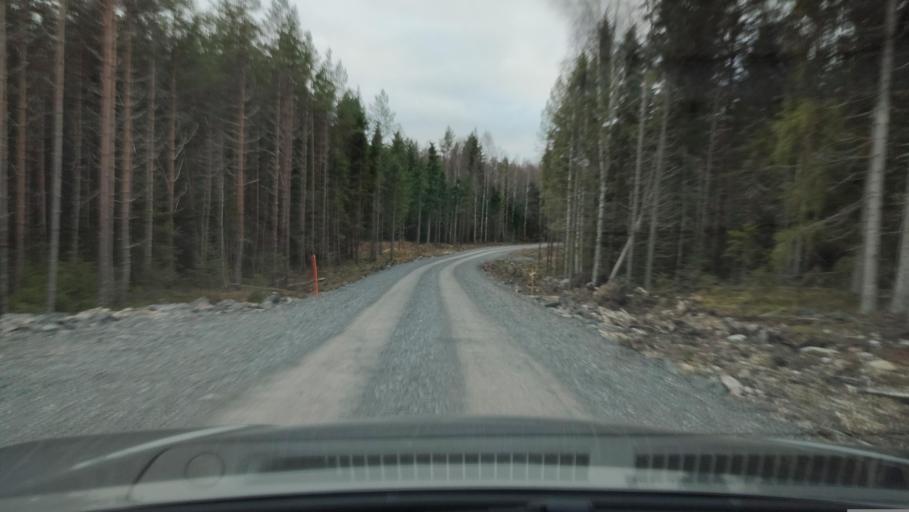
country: FI
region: Southern Ostrobothnia
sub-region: Suupohja
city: Karijoki
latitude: 62.1840
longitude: 21.5738
